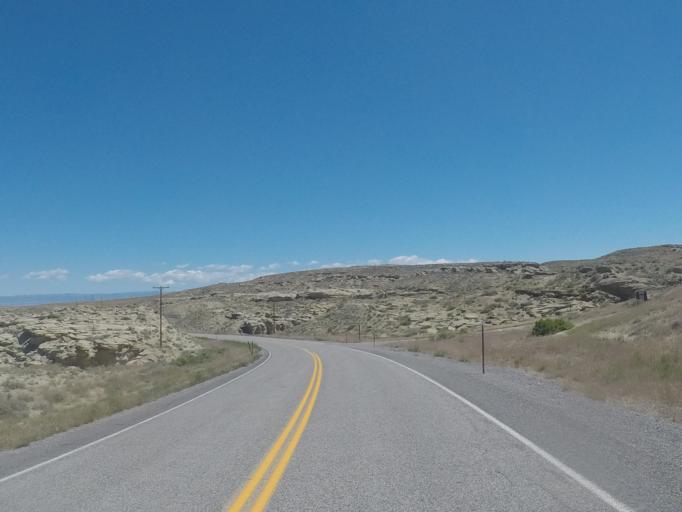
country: US
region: Wyoming
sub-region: Big Horn County
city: Lovell
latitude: 44.7850
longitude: -108.4707
